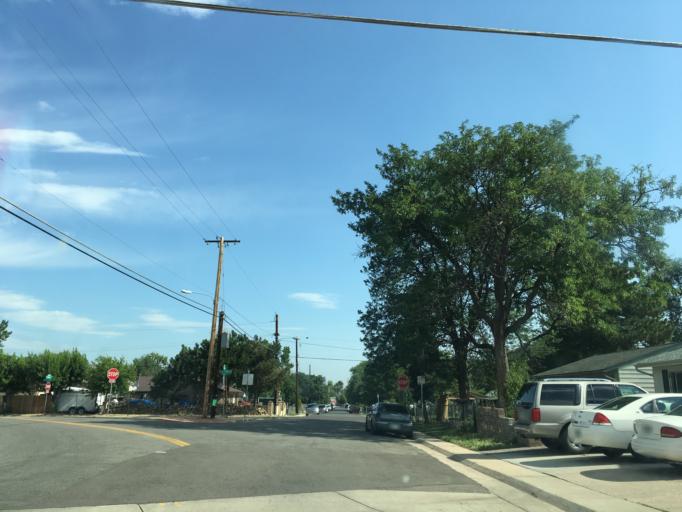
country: US
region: Colorado
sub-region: Jefferson County
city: Lakewood
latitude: 39.7035
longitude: -105.0391
